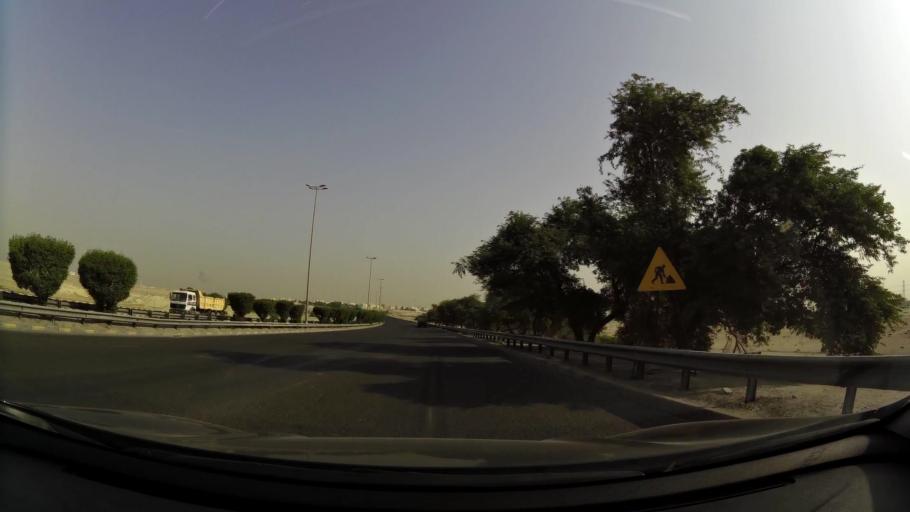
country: KW
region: Al Asimah
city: Ar Rabiyah
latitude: 29.2570
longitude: 47.8624
